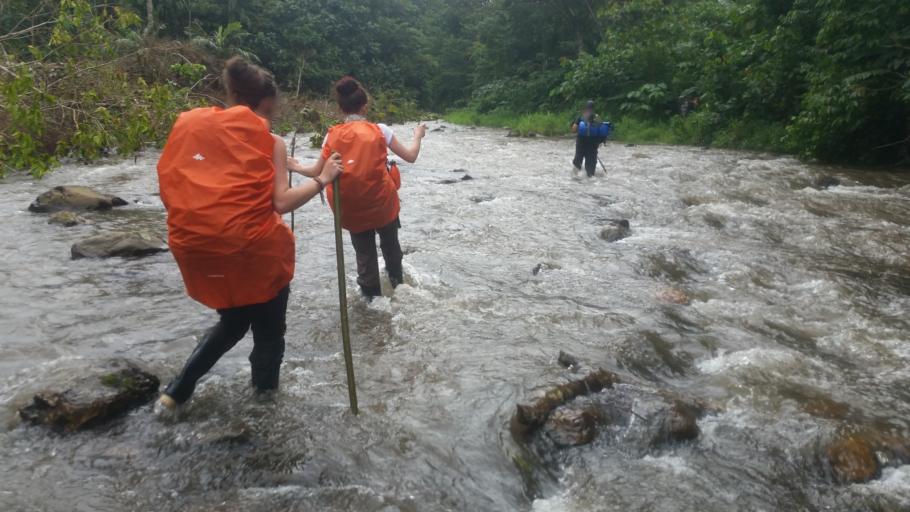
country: NI
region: Atlantico Norte (RAAN)
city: Bonanza
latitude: 14.0222
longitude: -84.7291
